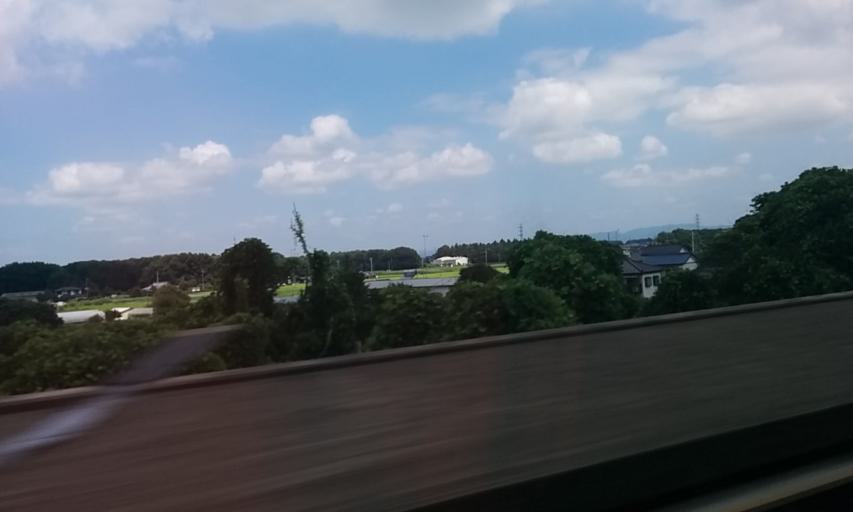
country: JP
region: Ibaraki
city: Koga
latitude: 36.2239
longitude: 139.7565
